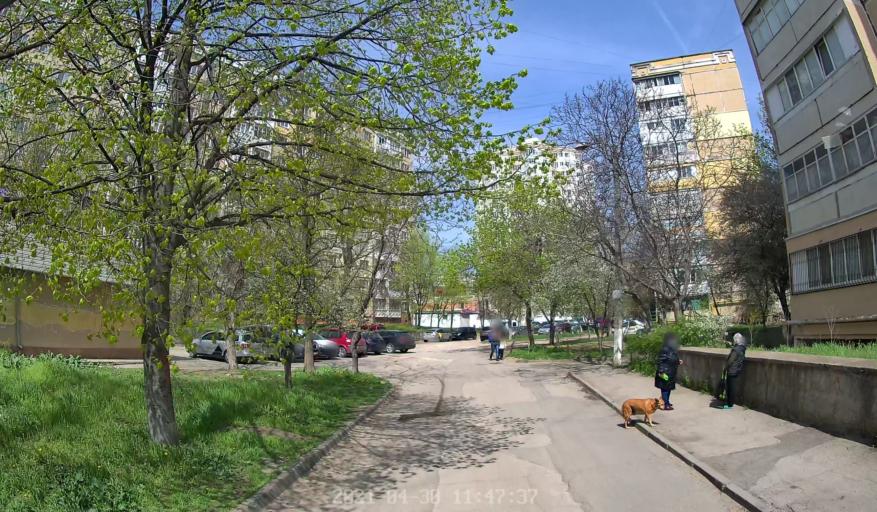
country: MD
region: Chisinau
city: Chisinau
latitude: 47.0385
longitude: 28.8949
